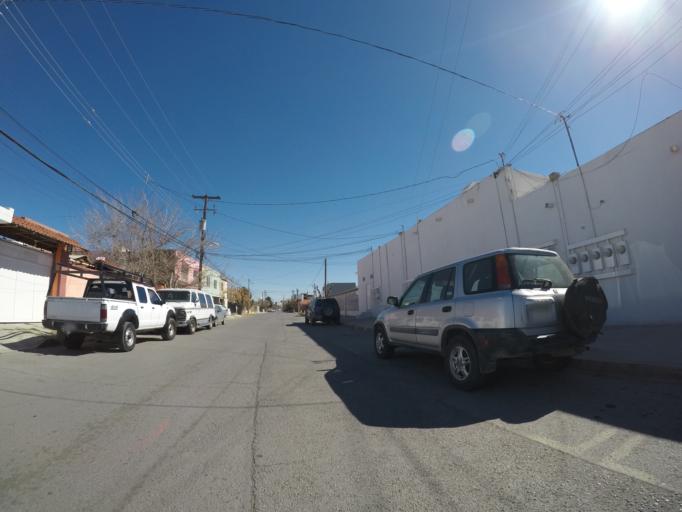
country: MX
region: Chihuahua
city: Ciudad Juarez
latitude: 31.7324
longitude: -106.4444
